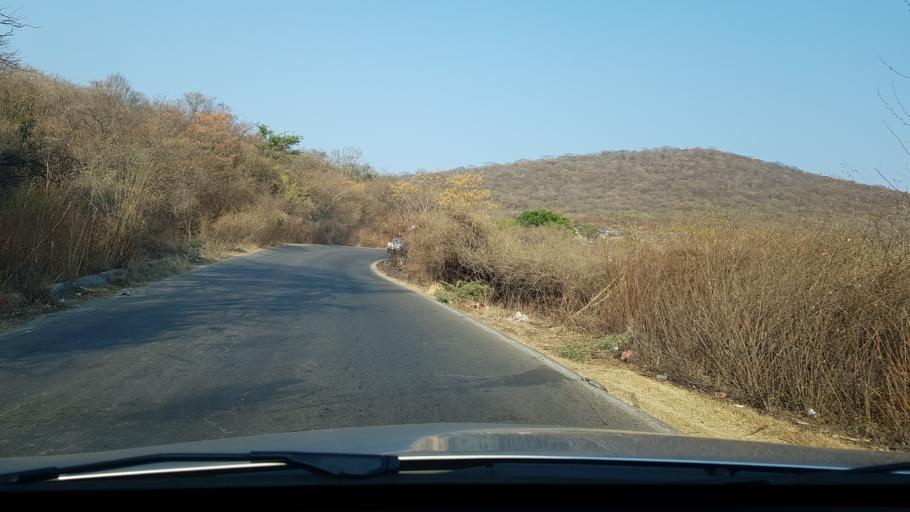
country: MX
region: Morelos
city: Tlaltizapan
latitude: 18.6581
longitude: -99.0427
